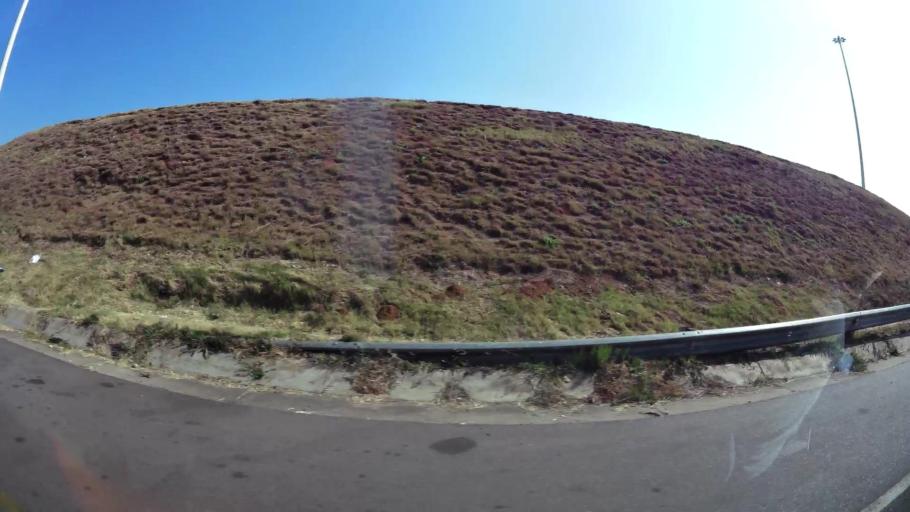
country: ZA
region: Gauteng
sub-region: City of Johannesburg Metropolitan Municipality
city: Modderfontein
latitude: -26.1333
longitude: 28.2241
